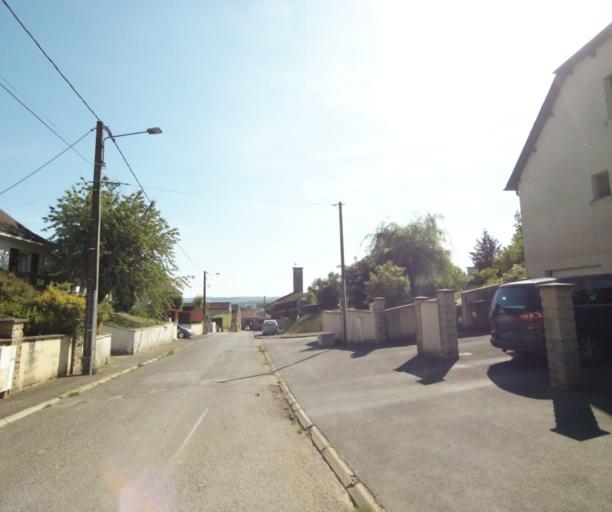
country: FR
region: Champagne-Ardenne
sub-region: Departement des Ardennes
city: Warcq
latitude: 49.7890
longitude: 4.6957
